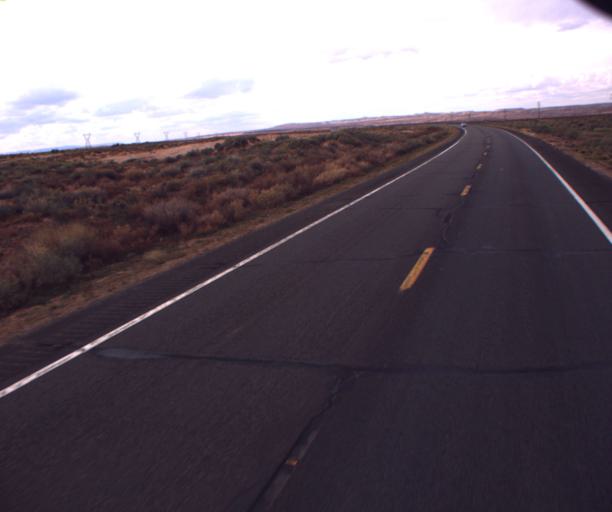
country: US
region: Arizona
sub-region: Apache County
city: Many Farms
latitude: 36.9414
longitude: -109.6468
